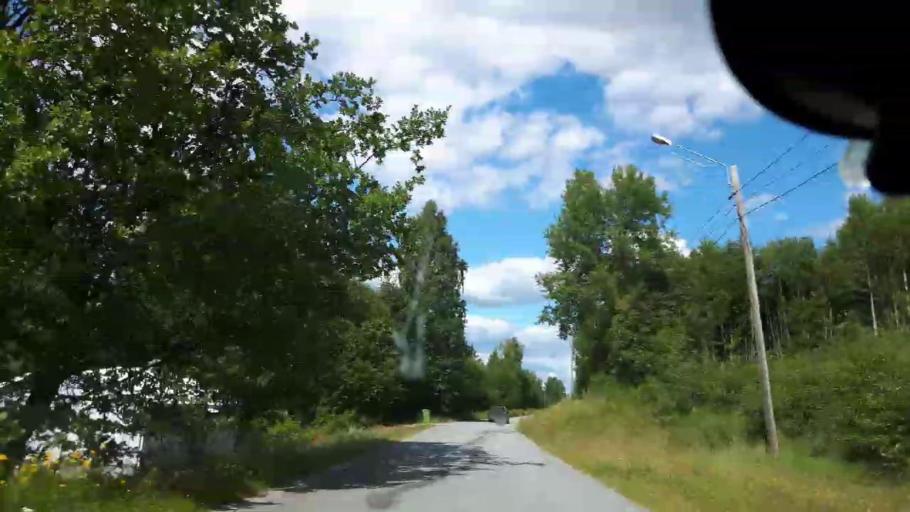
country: SE
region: Jaemtland
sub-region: Ragunda Kommun
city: Hammarstrand
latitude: 62.9438
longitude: 16.6910
